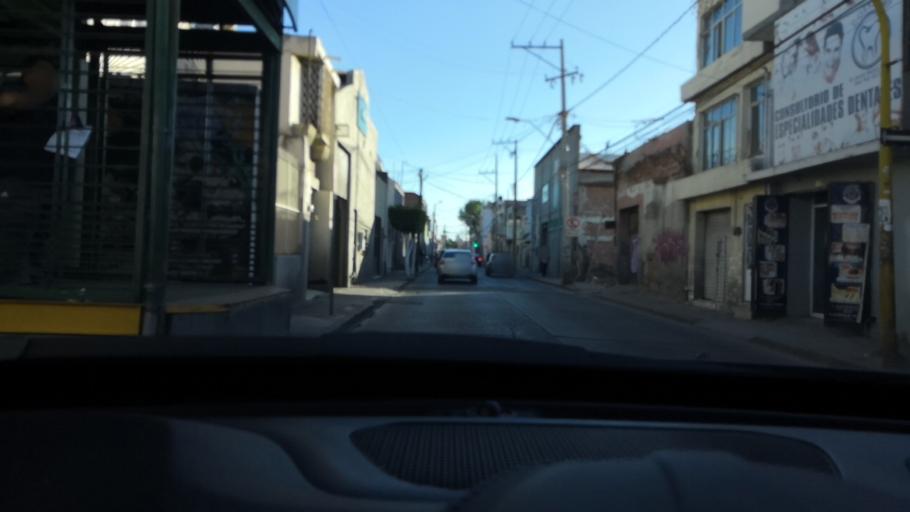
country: MX
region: Guanajuato
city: Leon
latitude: 21.1310
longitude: -101.6805
